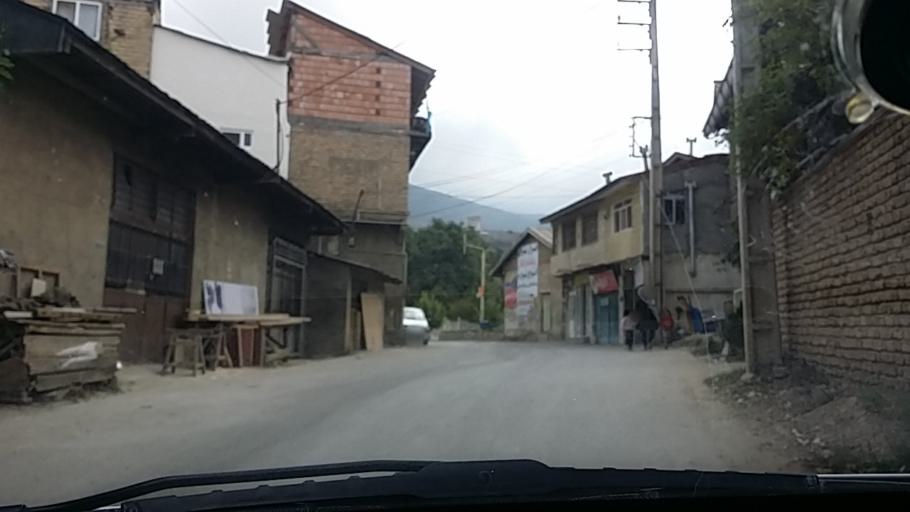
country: IR
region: Mazandaran
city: `Abbasabad
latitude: 36.5085
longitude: 51.1855
